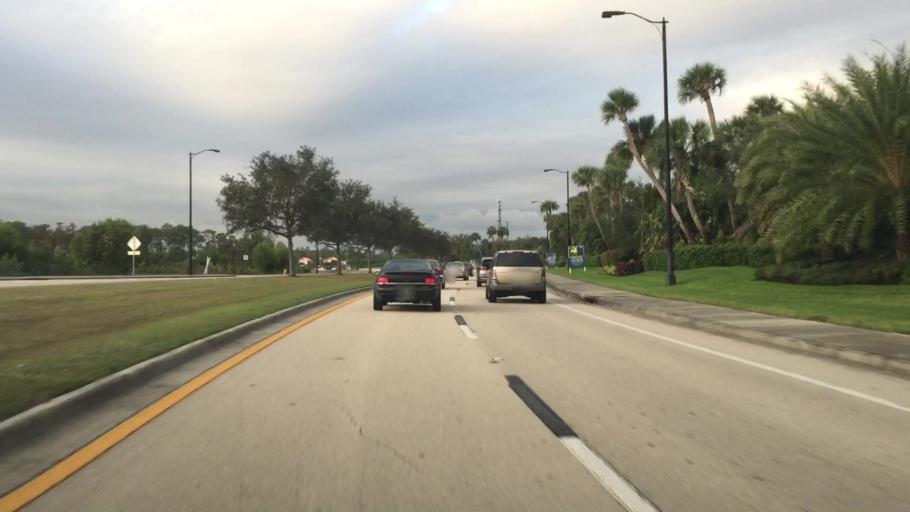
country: US
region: Florida
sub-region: Lee County
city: Gateway
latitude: 26.5680
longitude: -81.7835
